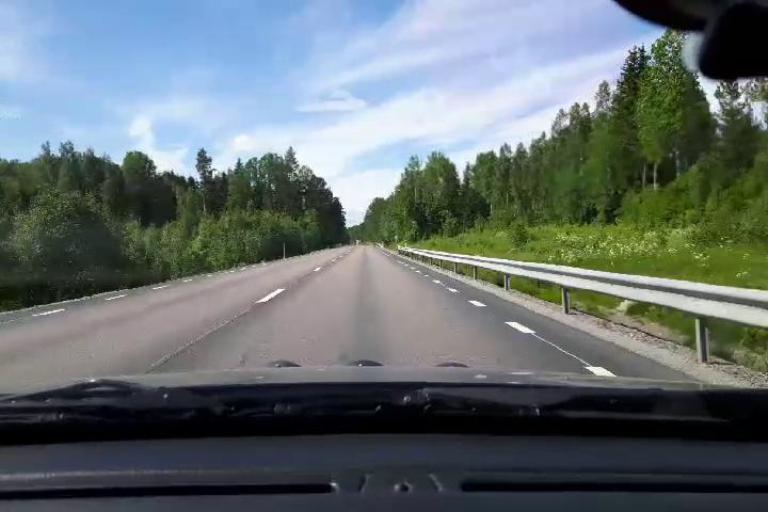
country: SE
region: Gaevleborg
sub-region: Bollnas Kommun
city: Kilafors
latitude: 61.1817
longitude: 16.7846
